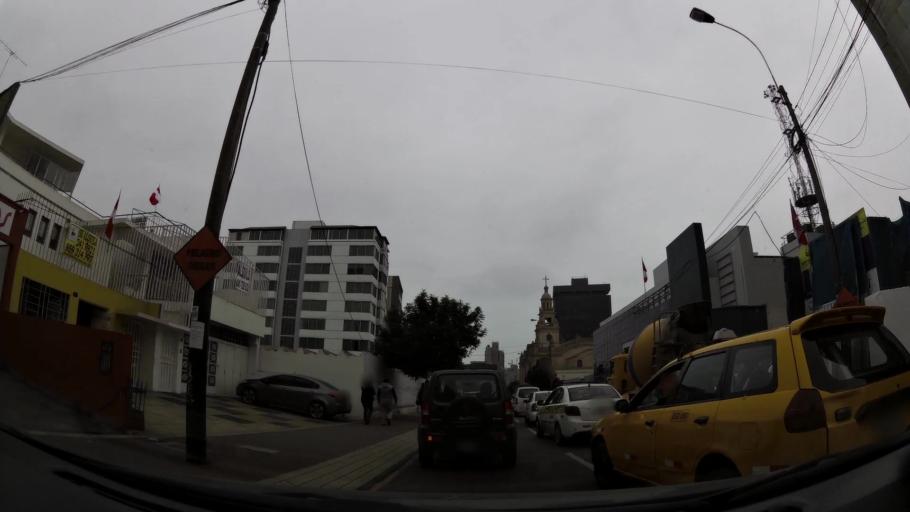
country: PE
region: Lima
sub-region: Lima
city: San Isidro
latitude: -12.0951
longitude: -77.0352
